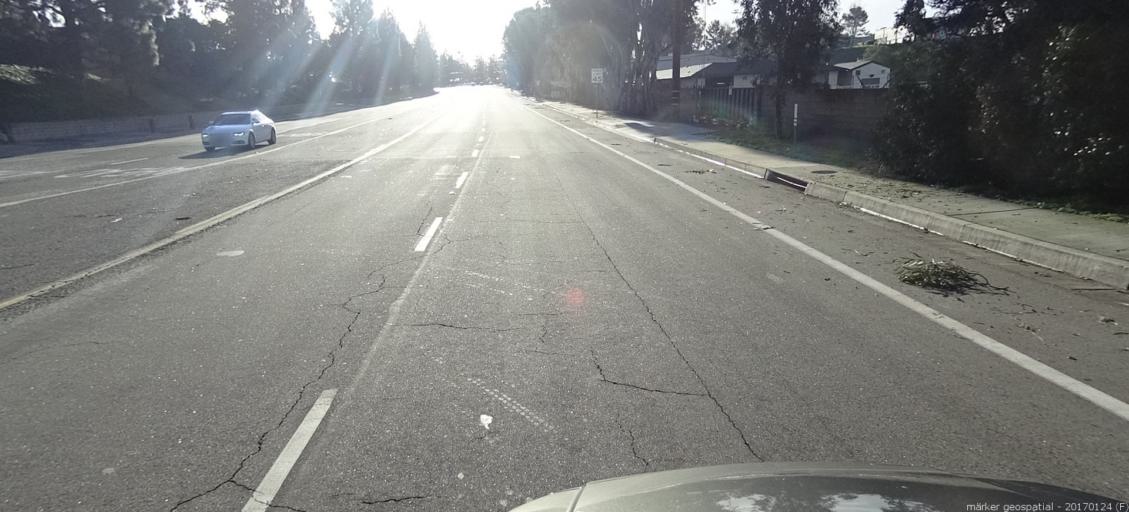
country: US
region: California
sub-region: Orange County
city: Laguna Hills
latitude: 33.6389
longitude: -117.7152
